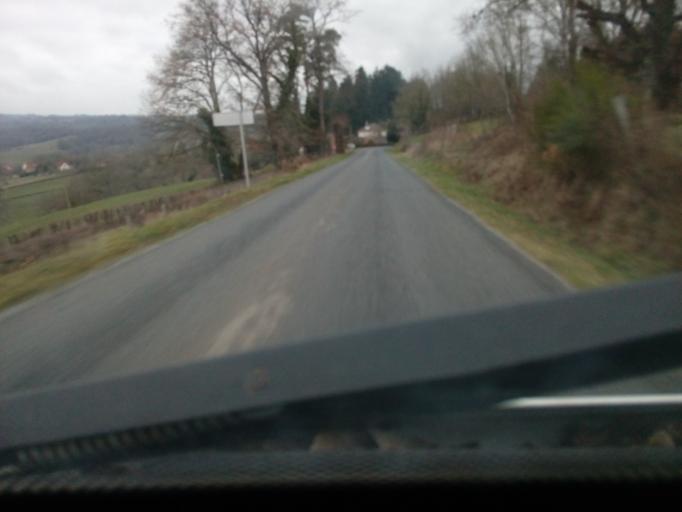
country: FR
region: Limousin
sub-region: Departement de la Creuse
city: Felletin
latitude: 45.8771
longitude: 2.1850
